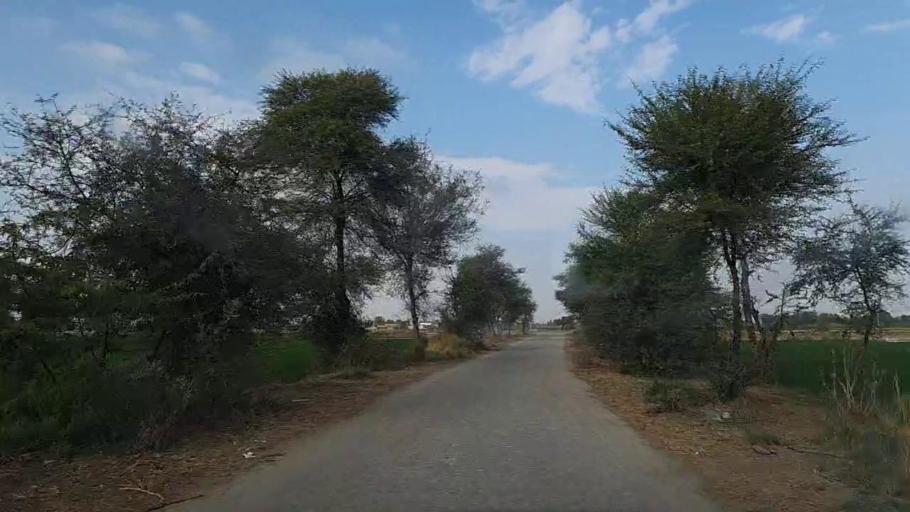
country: PK
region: Sindh
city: Sanghar
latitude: 26.2331
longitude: 69.0198
